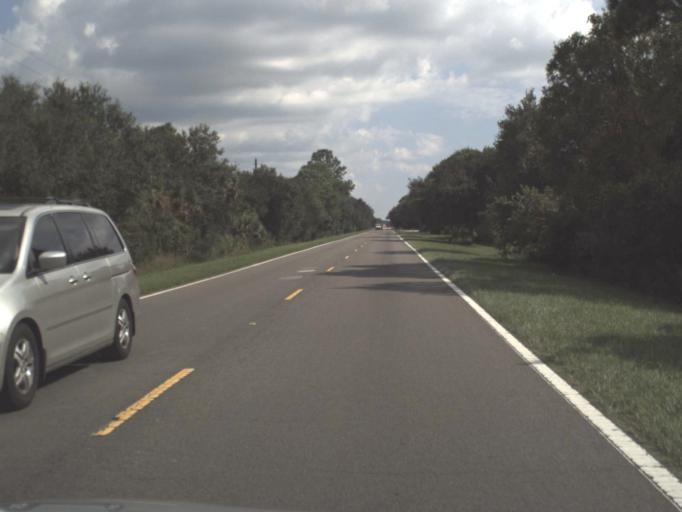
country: US
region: Florida
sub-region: Sarasota County
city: Plantation
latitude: 27.0960
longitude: -82.3417
